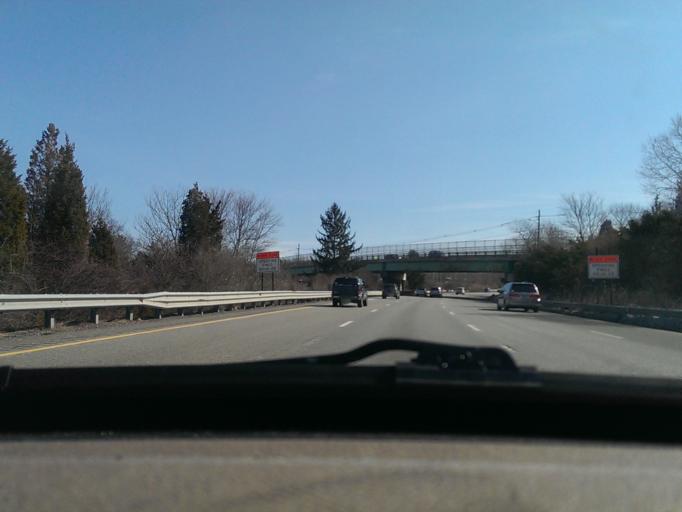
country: US
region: Massachusetts
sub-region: Bristol County
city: Swansea
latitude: 41.7273
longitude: -71.1871
